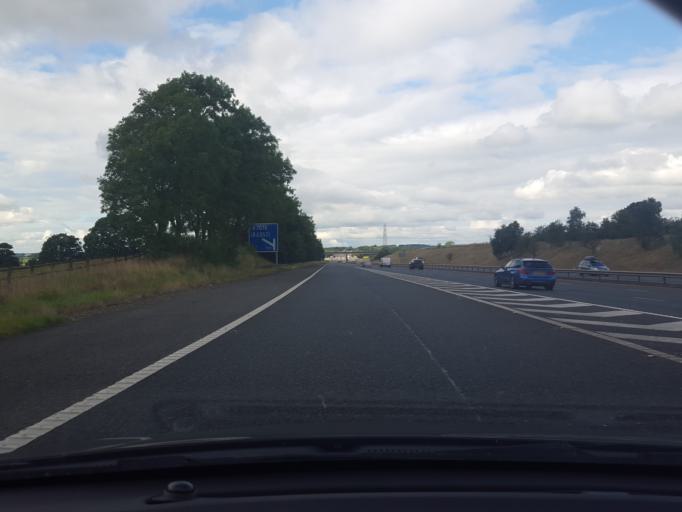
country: GB
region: Scotland
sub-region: Dumfries and Galloway
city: Gretna
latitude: 55.0106
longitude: -3.0916
